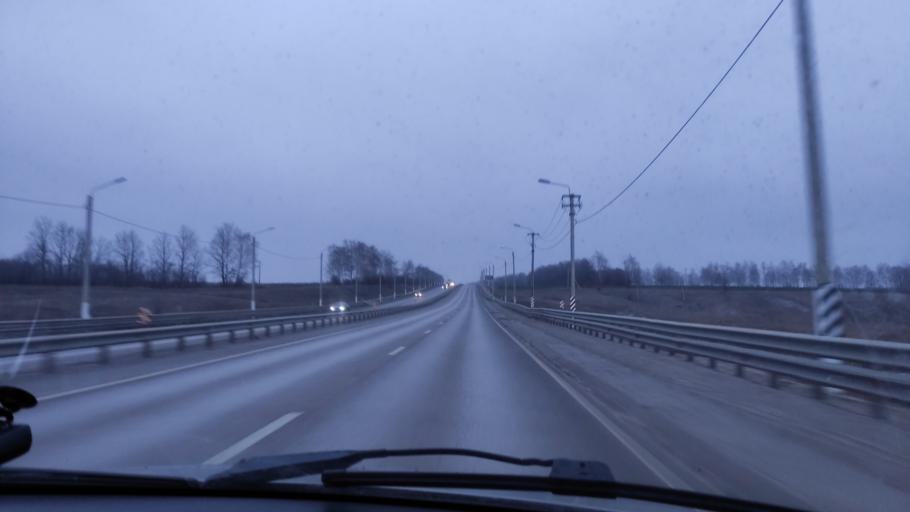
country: RU
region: Tambov
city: Komsomolets
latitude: 52.7285
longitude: 41.3273
